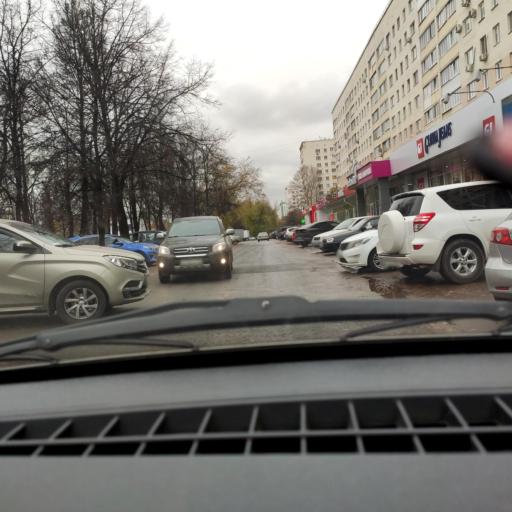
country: RU
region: Bashkortostan
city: Ufa
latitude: 54.7605
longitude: 56.0100
